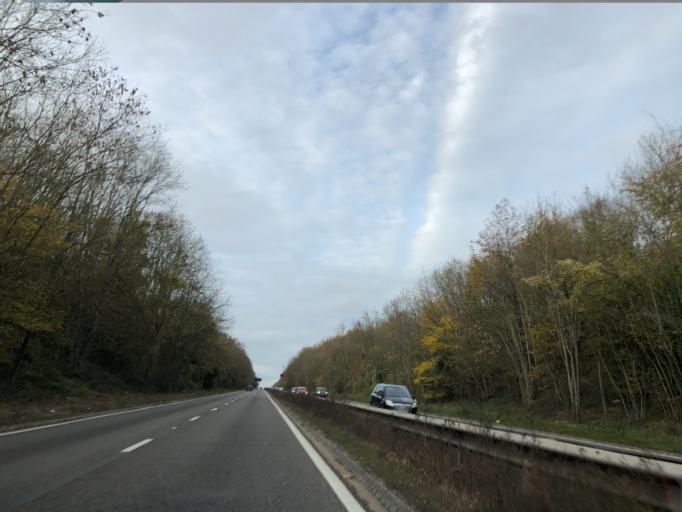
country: GB
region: England
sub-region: Buckinghamshire
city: Marlow
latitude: 51.5966
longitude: -0.7612
